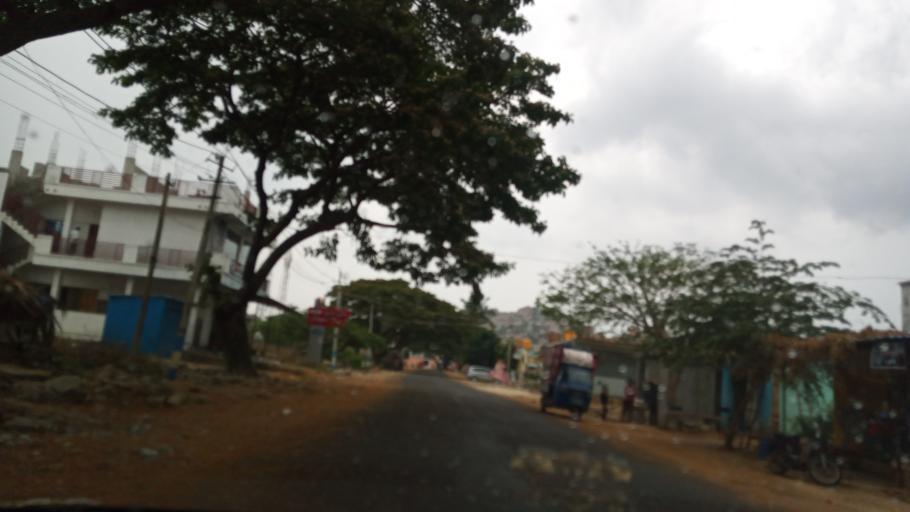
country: IN
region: Karnataka
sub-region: Kolar
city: Mulbagal
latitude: 13.1077
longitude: 78.3348
